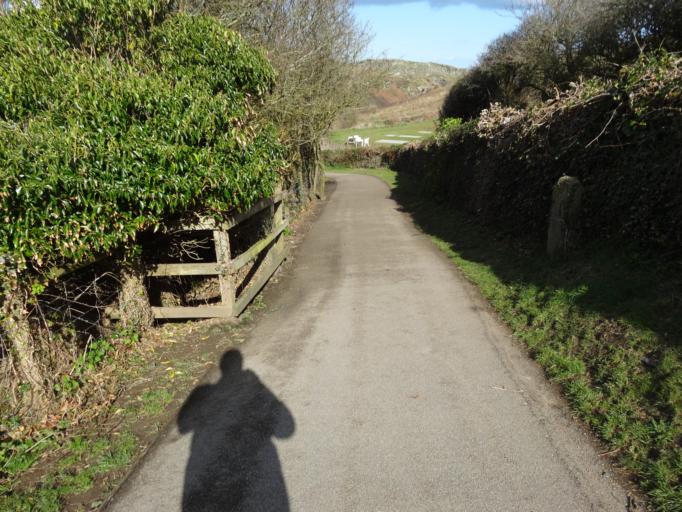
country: GB
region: England
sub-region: Cornwall
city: Tintagel
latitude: 50.6644
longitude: -4.7549
